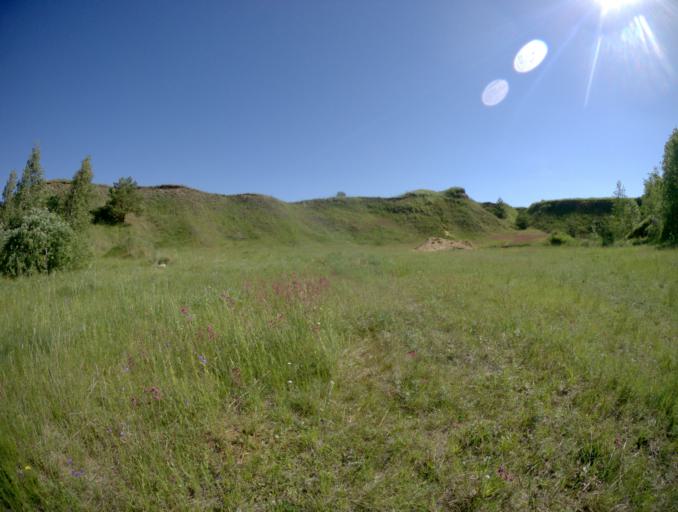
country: RU
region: Ivanovo
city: Gavrilov Posad
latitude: 56.5317
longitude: 40.2006
